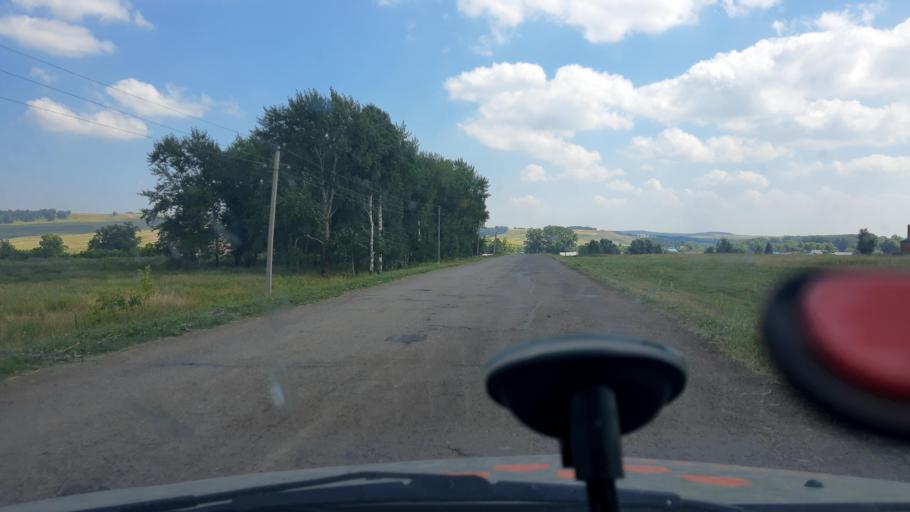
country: RU
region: Bashkortostan
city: Chekmagush
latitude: 54.8837
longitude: 54.5991
